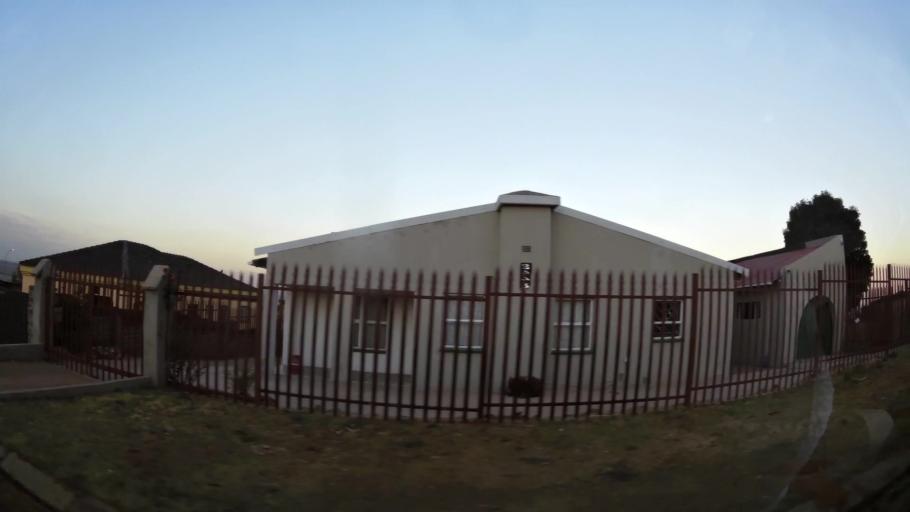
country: ZA
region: Gauteng
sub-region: West Rand District Municipality
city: Randfontein
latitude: -26.2047
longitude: 27.7198
